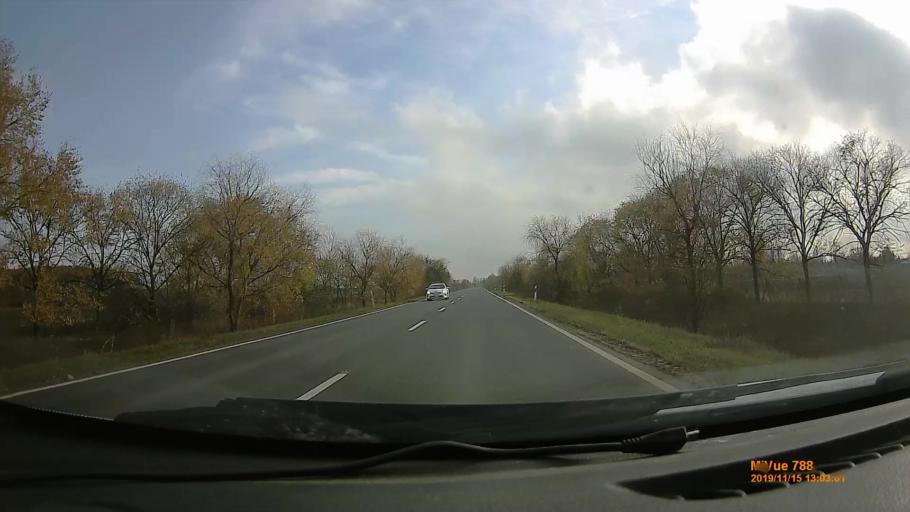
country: HU
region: Bekes
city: Gyula
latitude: 46.6472
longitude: 21.2411
